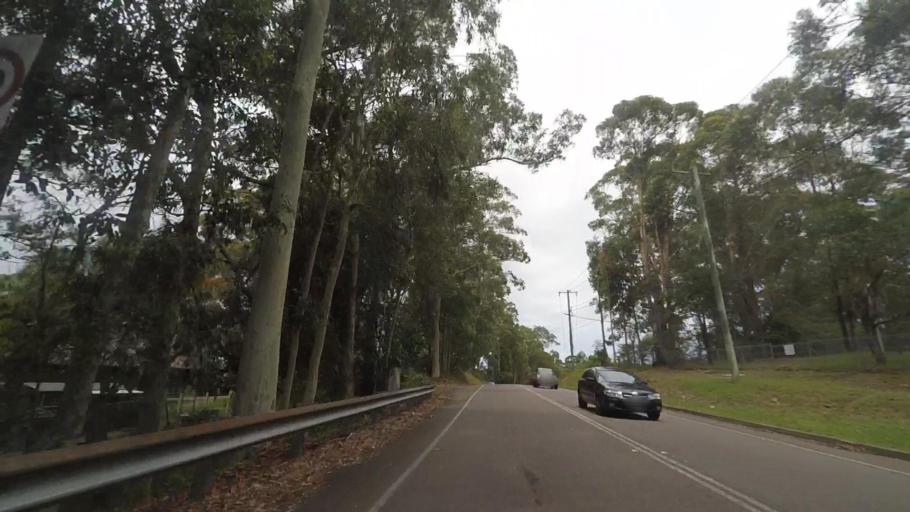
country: AU
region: New South Wales
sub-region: Wyong Shire
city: Chittaway Bay
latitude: -33.3397
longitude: 151.4193
